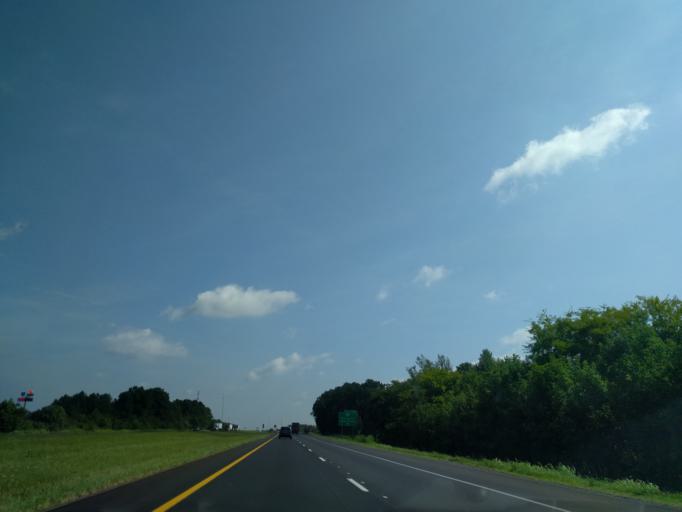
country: US
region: Tennessee
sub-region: Sumner County
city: White House
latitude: 36.4627
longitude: -86.6868
